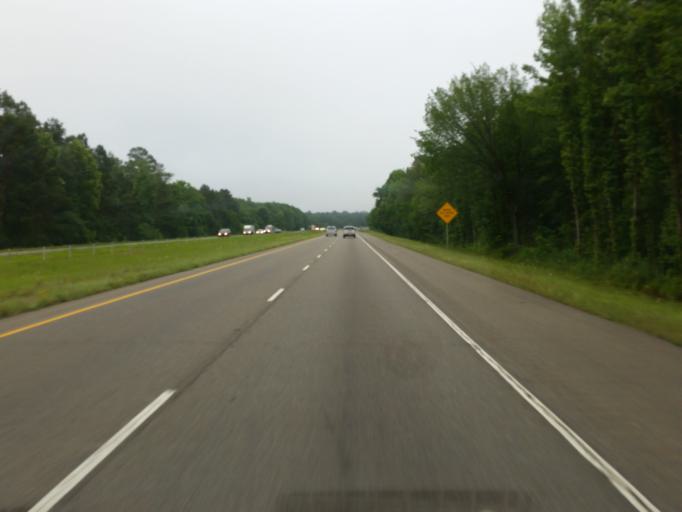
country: US
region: Louisiana
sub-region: Bossier Parish
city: Haughton
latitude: 32.5692
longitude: -93.4883
